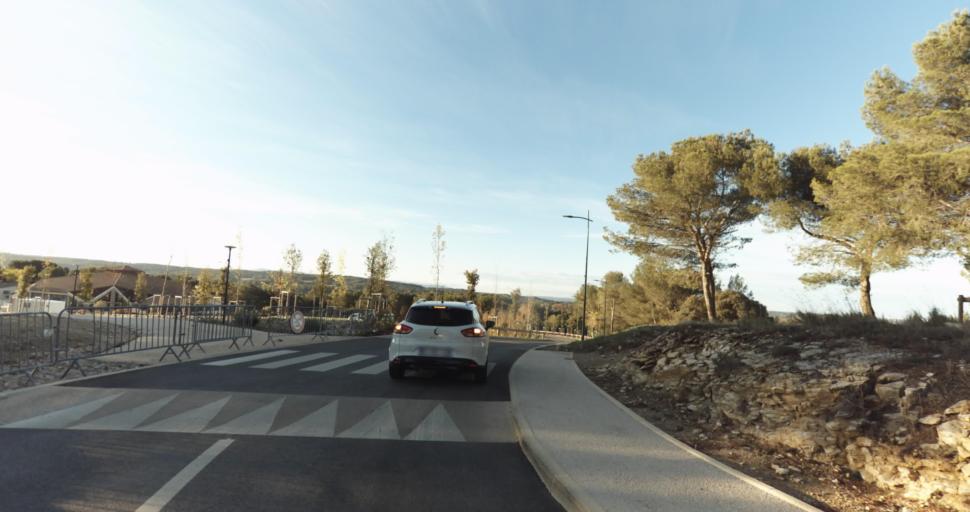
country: FR
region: Provence-Alpes-Cote d'Azur
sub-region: Departement des Bouches-du-Rhone
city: Venelles
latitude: 43.5969
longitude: 5.4923
